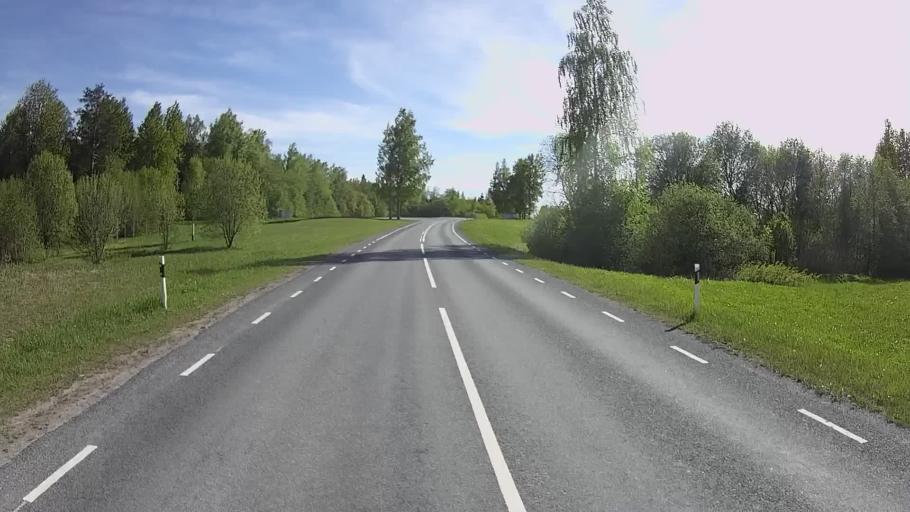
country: EE
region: Vorumaa
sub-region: Antsla vald
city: Vana-Antsla
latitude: 57.9597
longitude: 26.4526
